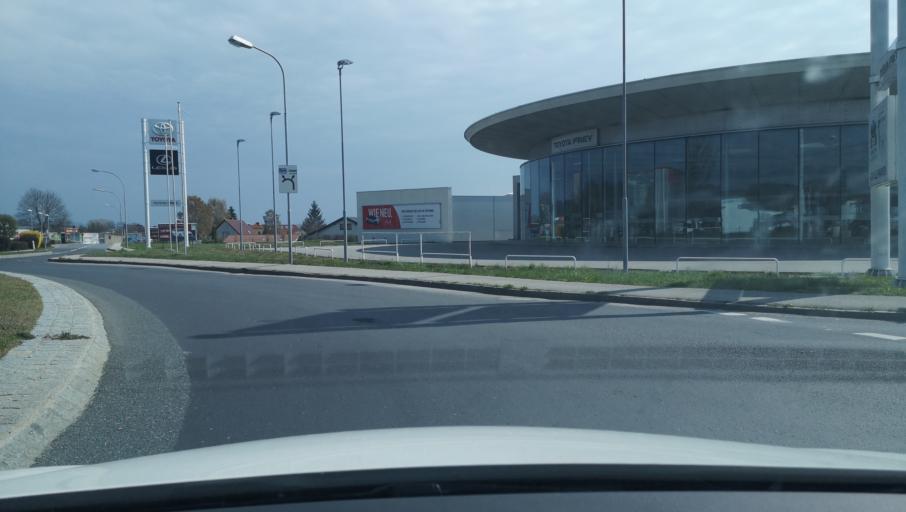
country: AT
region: Lower Austria
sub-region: Politischer Bezirk Amstetten
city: Winklarn
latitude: 48.1079
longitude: 14.8357
